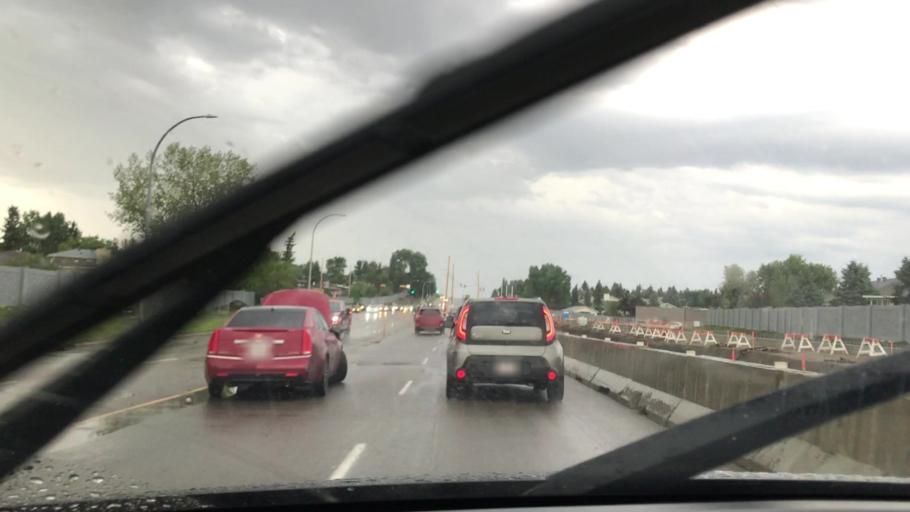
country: CA
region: Alberta
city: Edmonton
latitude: 53.4638
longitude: -113.4353
